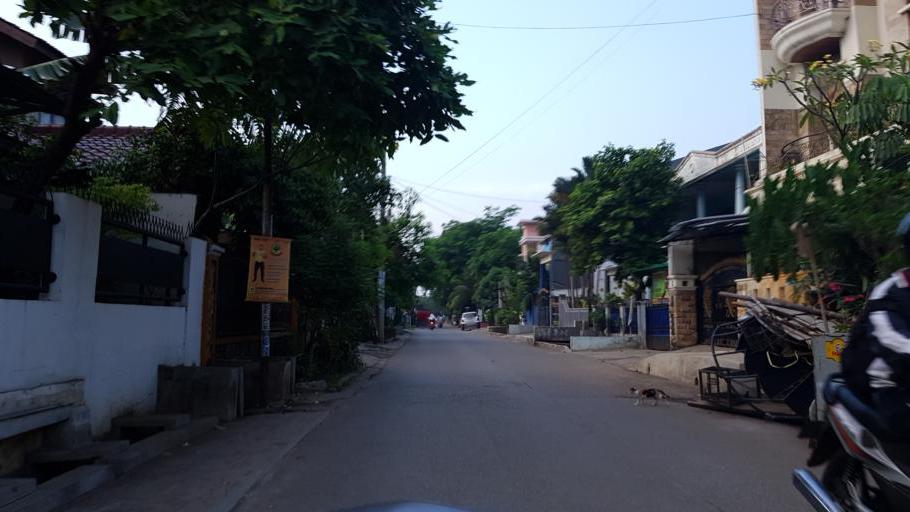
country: ID
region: West Java
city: Bekasi
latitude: -6.2729
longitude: 106.9474
